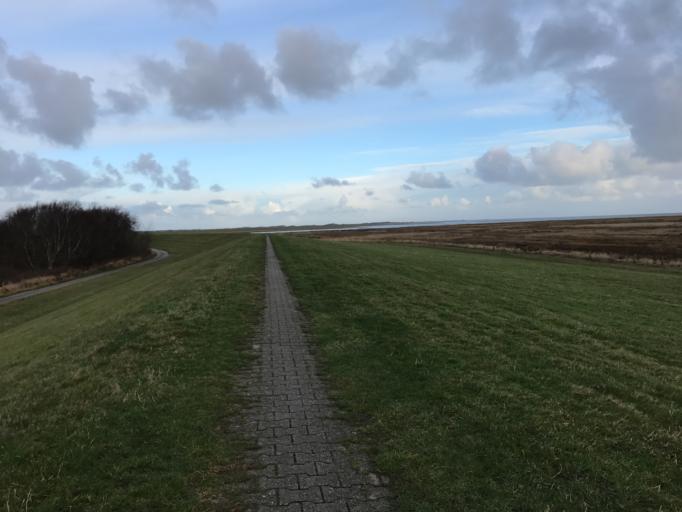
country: DE
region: Lower Saxony
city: Borkum
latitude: 53.5784
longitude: 6.7127
